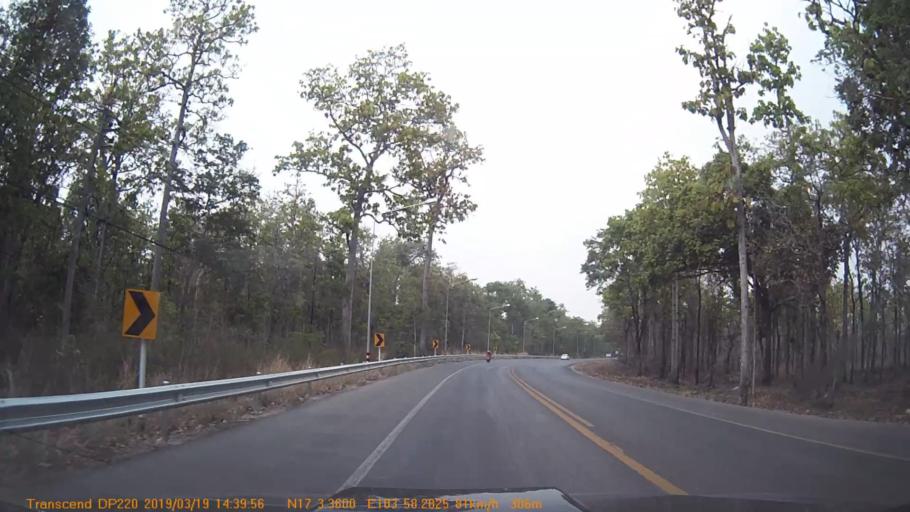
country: TH
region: Sakon Nakhon
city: Phu Phan
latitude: 17.0564
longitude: 103.9714
